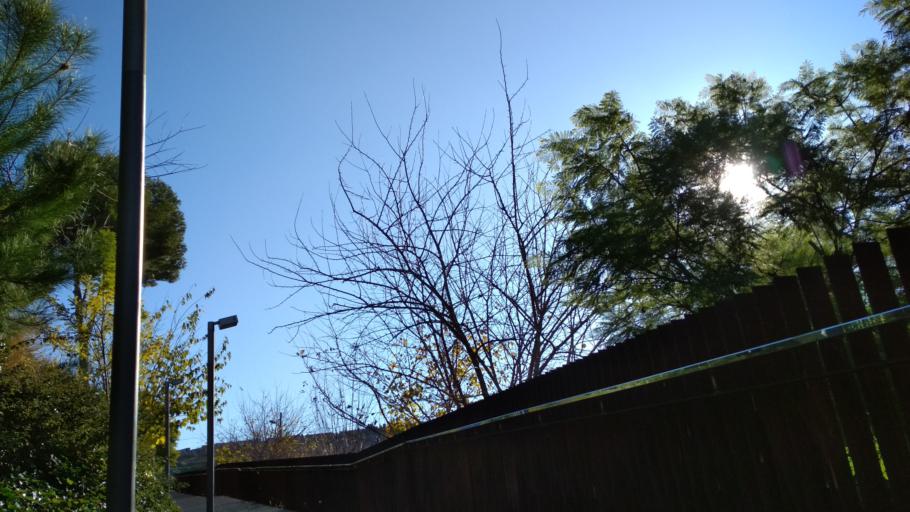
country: ES
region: Catalonia
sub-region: Provincia de Barcelona
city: Sants-Montjuic
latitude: 41.3607
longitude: 2.1425
